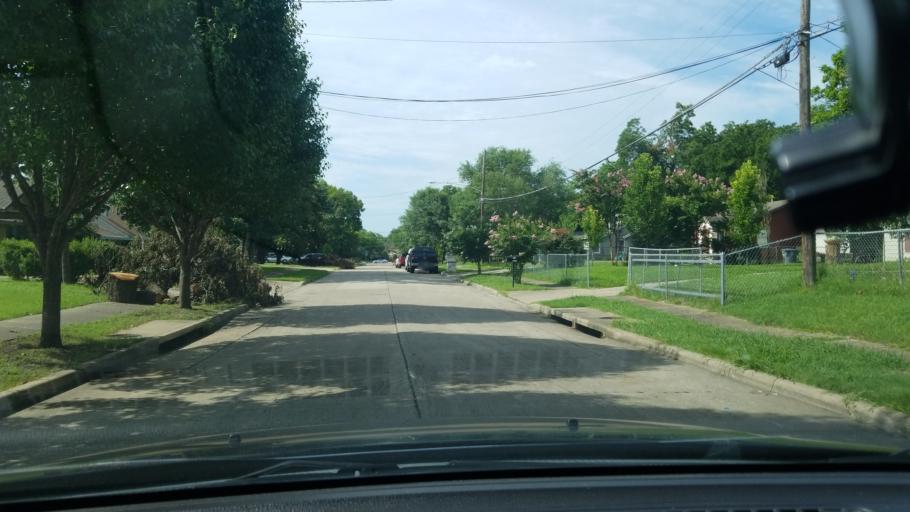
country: US
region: Texas
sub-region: Dallas County
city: Balch Springs
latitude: 32.7655
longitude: -96.6700
